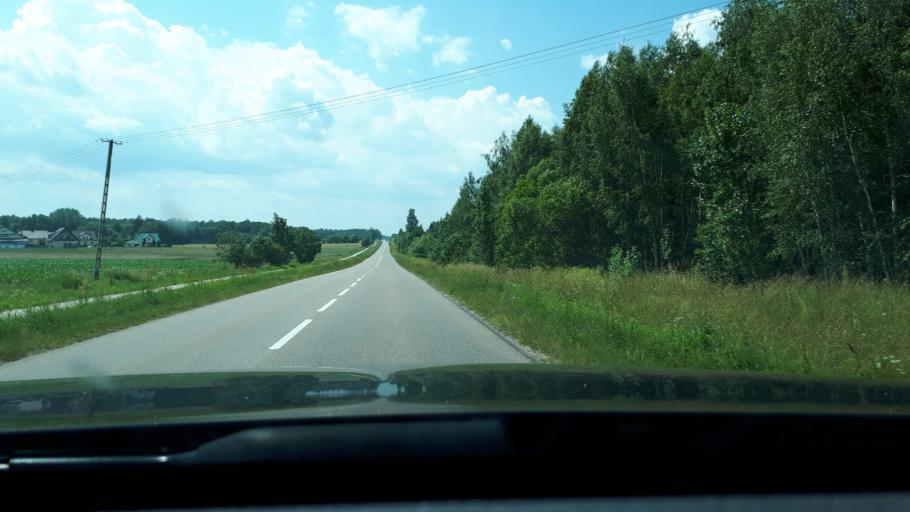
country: PL
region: Podlasie
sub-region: Powiat bialostocki
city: Choroszcz
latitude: 53.1284
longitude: 23.0056
